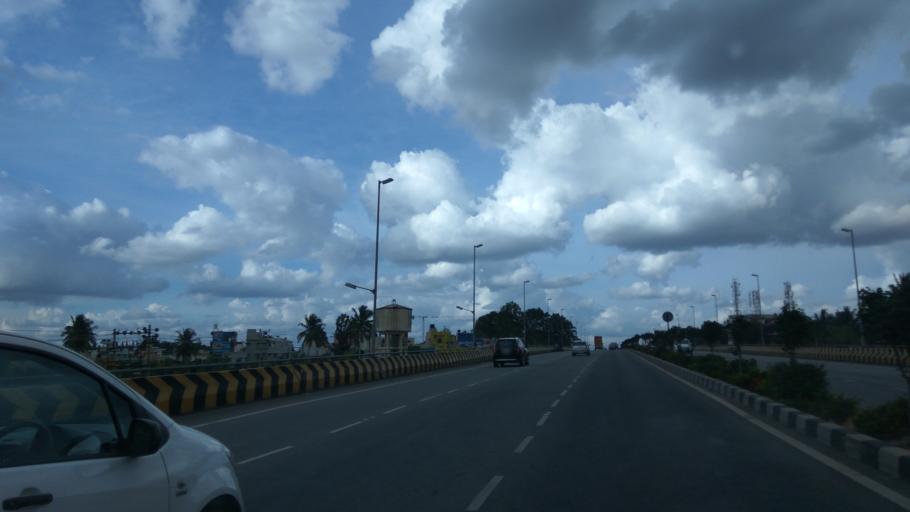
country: IN
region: Karnataka
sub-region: Bangalore Urban
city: Yelahanka
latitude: 13.1092
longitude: 77.6034
